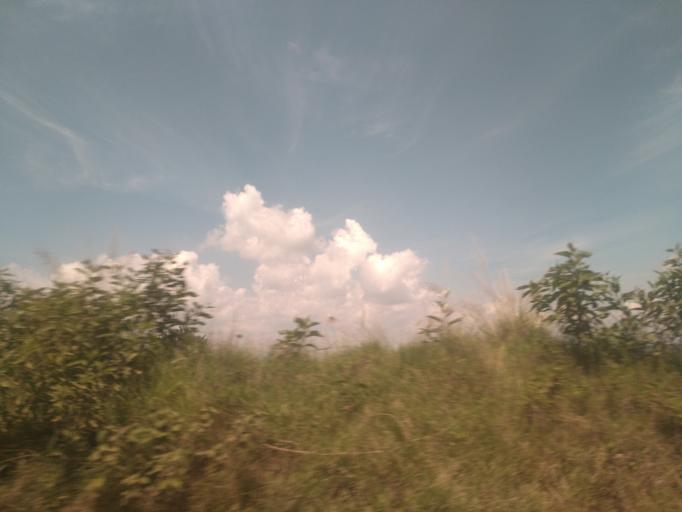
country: UG
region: Central Region
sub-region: Wakiso District
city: Entebbe
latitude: 0.0383
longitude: 32.4270
